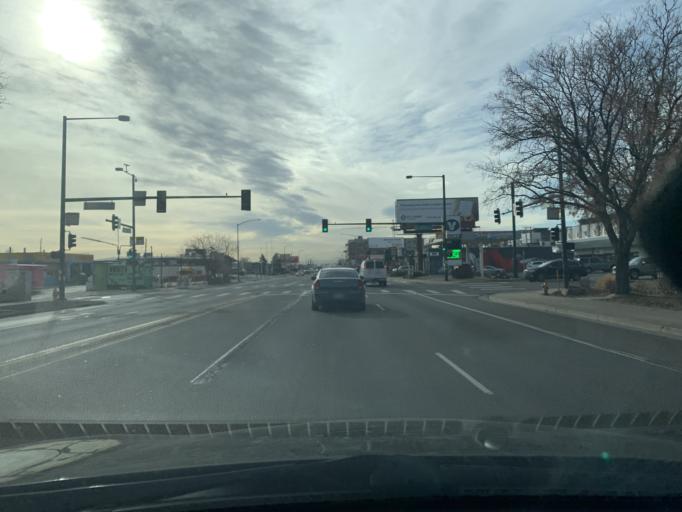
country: US
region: Colorado
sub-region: Jefferson County
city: Edgewater
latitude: 39.7480
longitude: -105.0253
